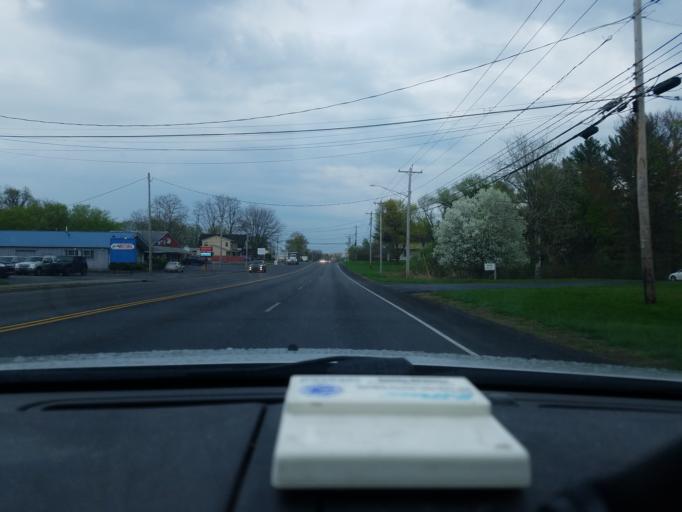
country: US
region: New York
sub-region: Onondaga County
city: North Syracuse
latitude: 43.1251
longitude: -76.1035
